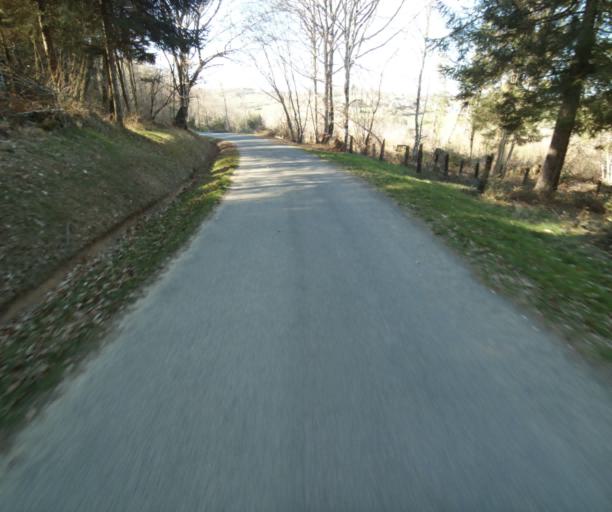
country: FR
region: Limousin
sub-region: Departement de la Correze
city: Chamboulive
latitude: 45.4158
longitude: 1.6504
